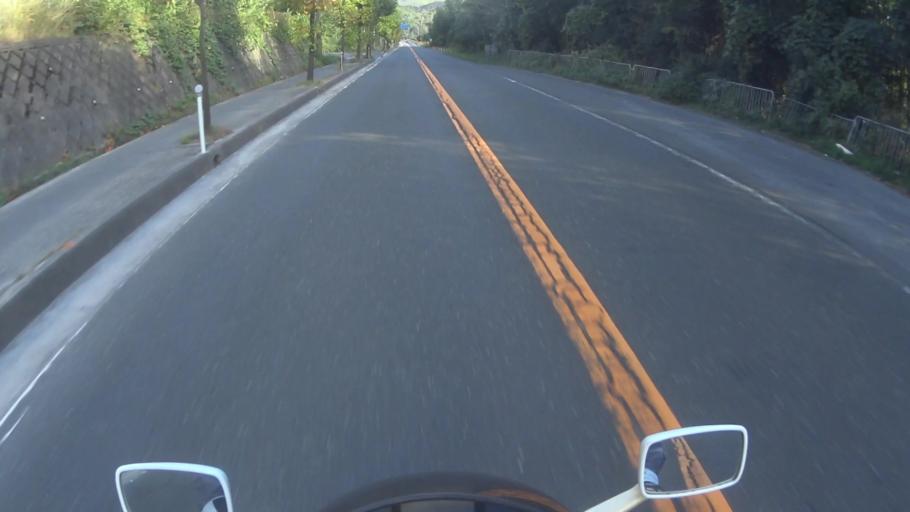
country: JP
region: Kyoto
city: Maizuru
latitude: 35.4278
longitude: 135.2363
